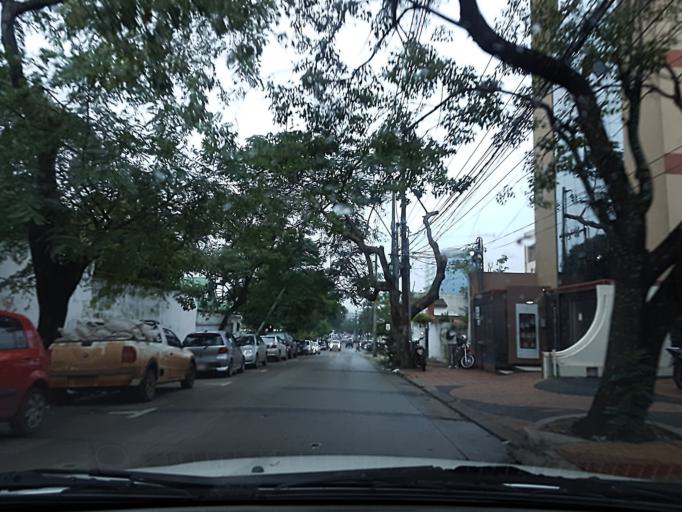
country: PY
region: Central
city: Lambare
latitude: -25.2980
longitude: -57.5799
